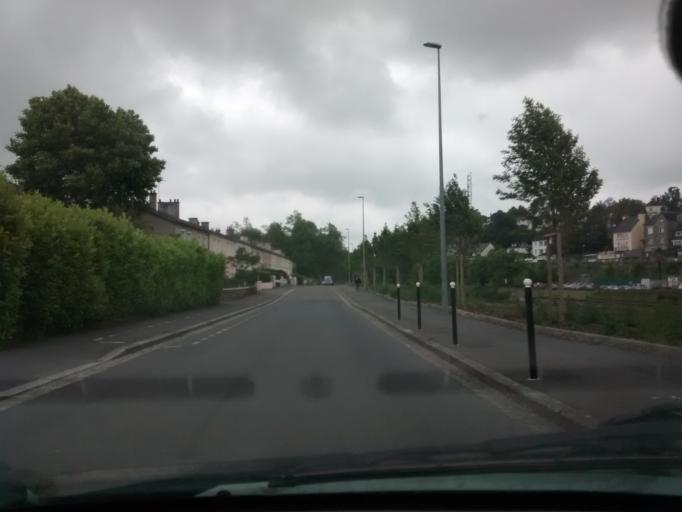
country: FR
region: Lower Normandy
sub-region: Departement de la Manche
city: Agneaux
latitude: 49.1145
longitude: -1.1005
